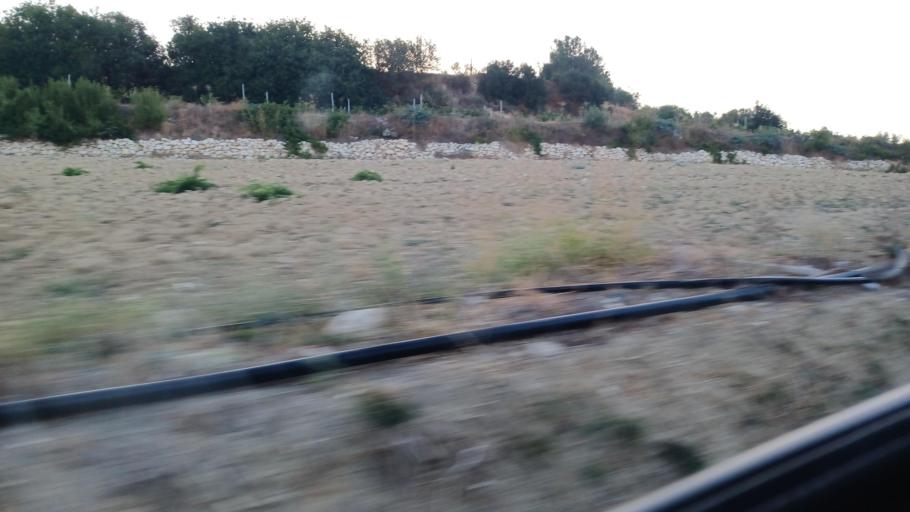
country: CY
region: Pafos
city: Mesogi
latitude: 34.8313
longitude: 32.5650
